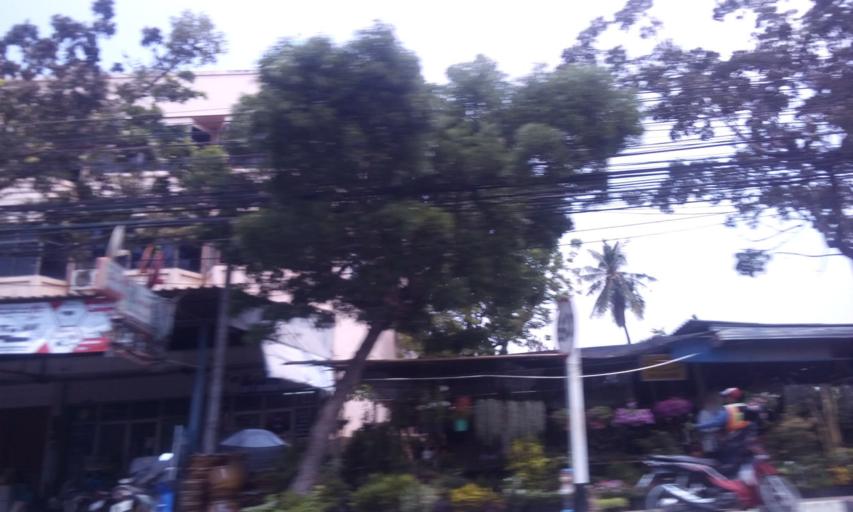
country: TH
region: Chachoengsao
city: Chachoengsao
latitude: 13.6770
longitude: 101.0835
